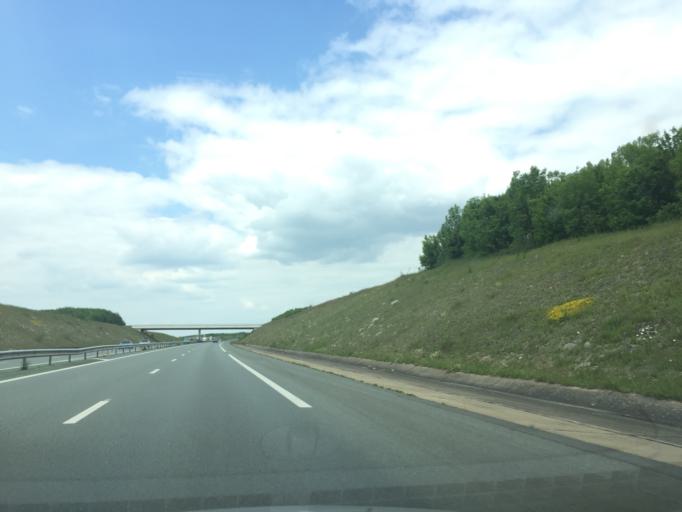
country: FR
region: Poitou-Charentes
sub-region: Departement des Deux-Sevres
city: Saint-Gelais
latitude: 46.3851
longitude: -0.3679
